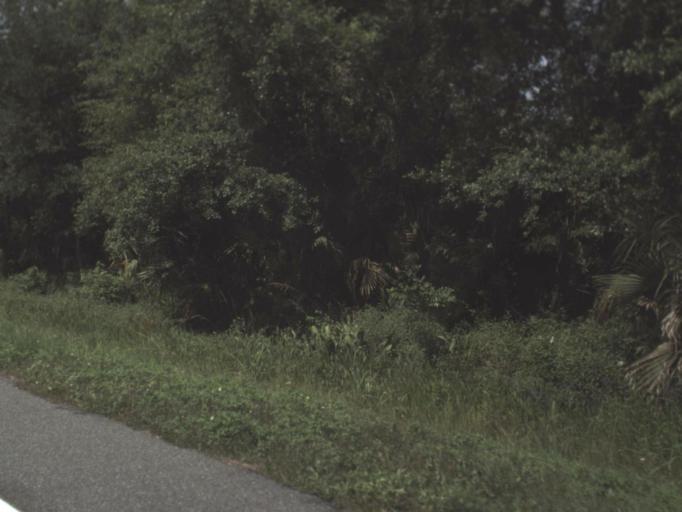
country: US
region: Florida
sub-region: Taylor County
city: Steinhatchee
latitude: 29.8508
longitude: -83.3102
